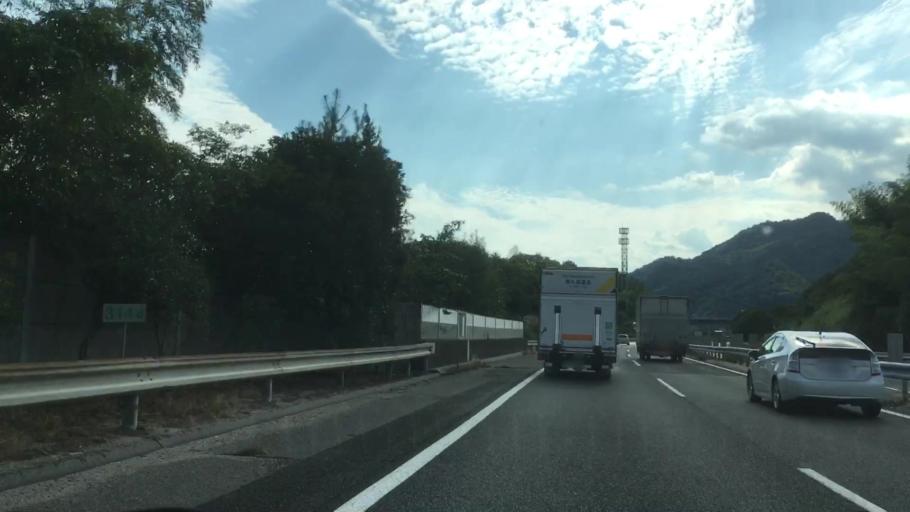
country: JP
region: Hiroshima
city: Ono-hara
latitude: 34.3033
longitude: 132.2774
